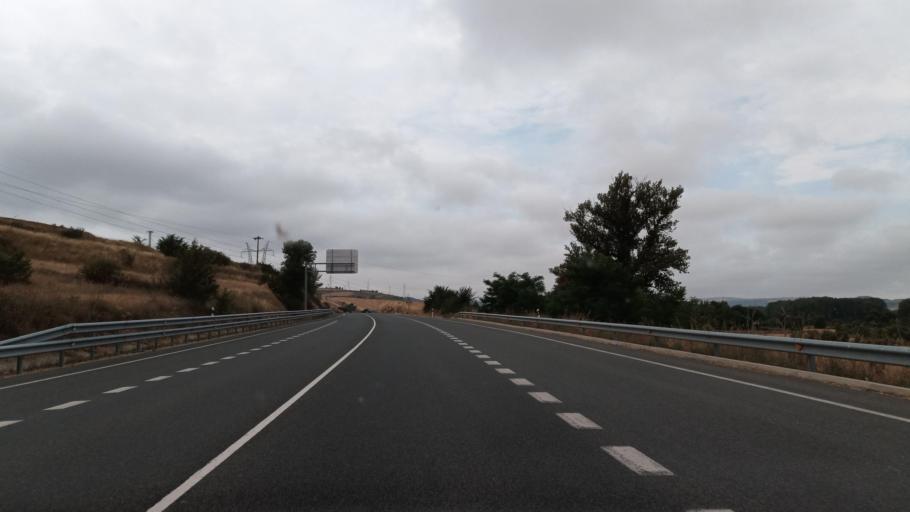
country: ES
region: Castille and Leon
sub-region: Provincia de Burgos
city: Castil de Peones
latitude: 42.4857
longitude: -3.3793
